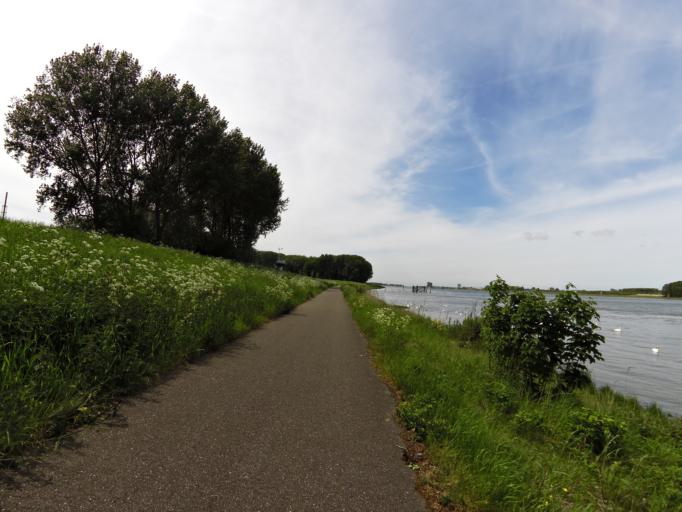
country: NL
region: South Holland
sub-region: Gemeente Maassluis
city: Maassluis
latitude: 51.8998
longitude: 4.2738
